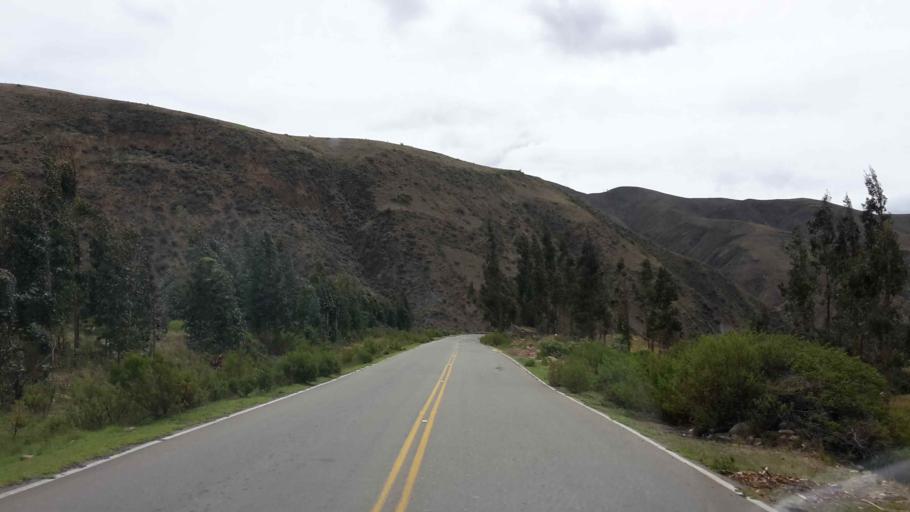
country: BO
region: Cochabamba
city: Colomi
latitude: -17.4134
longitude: -65.7708
